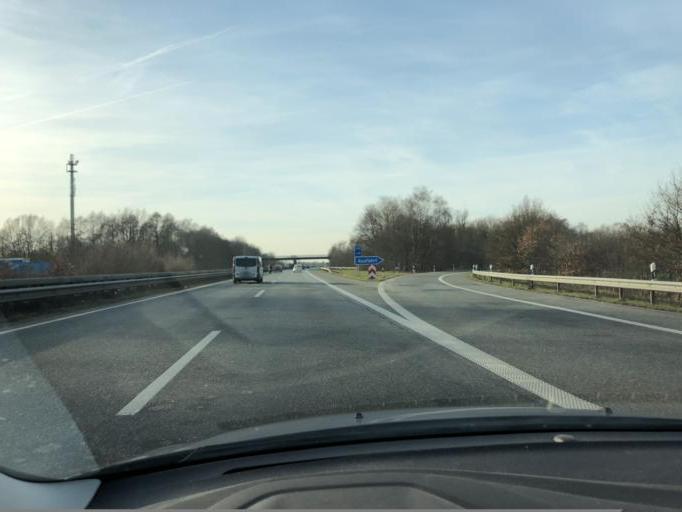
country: DE
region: Lower Saxony
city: Hatten
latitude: 53.0623
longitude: 8.3591
